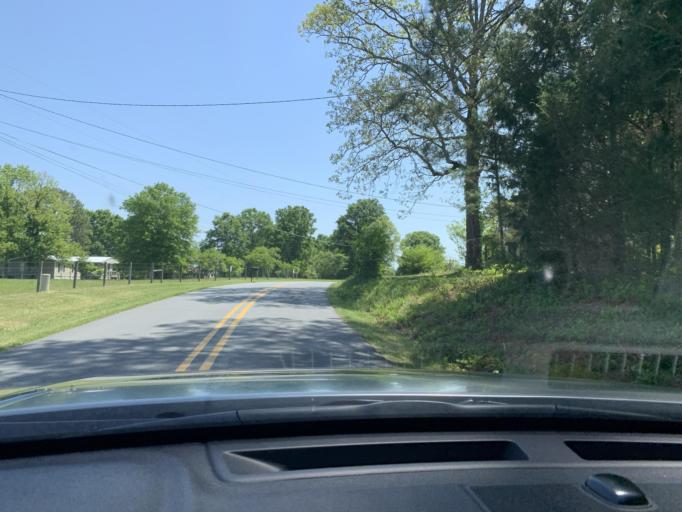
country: US
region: Georgia
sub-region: Polk County
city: Aragon
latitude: 34.0713
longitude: -85.0979
